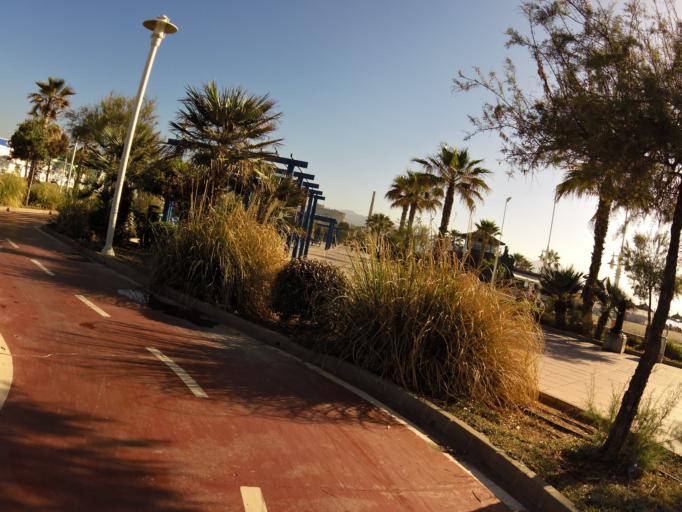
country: ES
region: Andalusia
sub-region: Provincia de Malaga
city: Malaga
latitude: 36.6859
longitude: -4.4446
